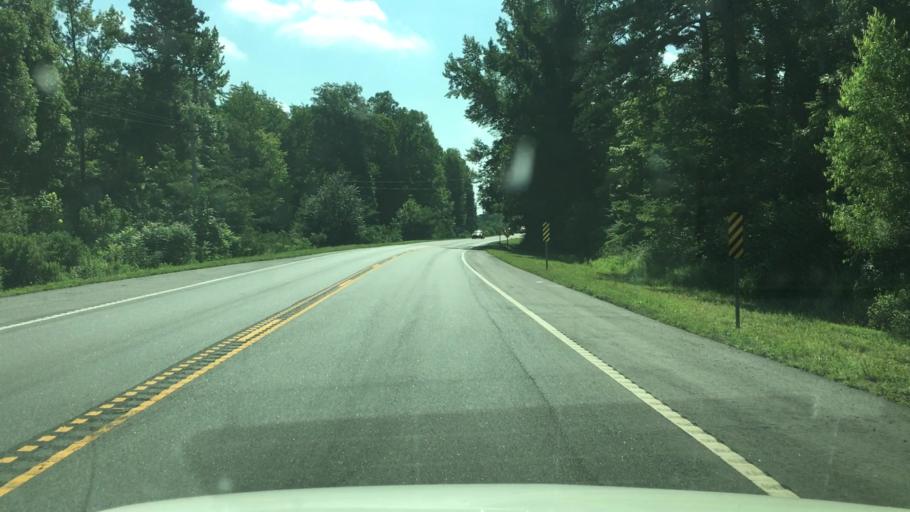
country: US
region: Arkansas
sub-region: Garland County
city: Rockwell
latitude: 34.5173
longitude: -93.3027
